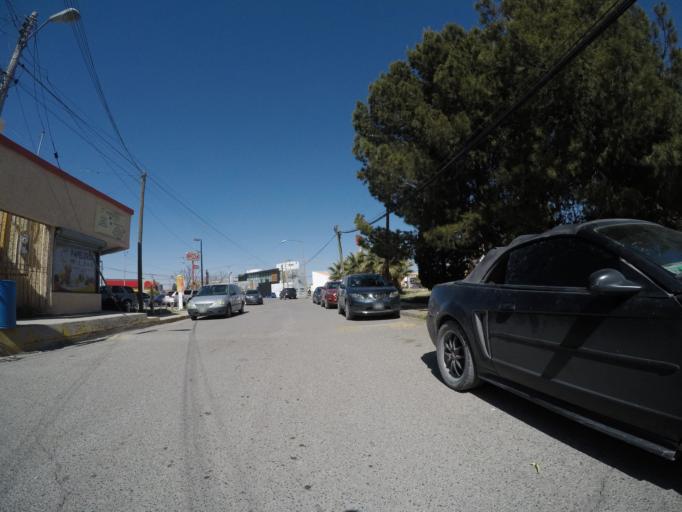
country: MX
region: Chihuahua
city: Ciudad Juarez
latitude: 31.6920
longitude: -106.4188
